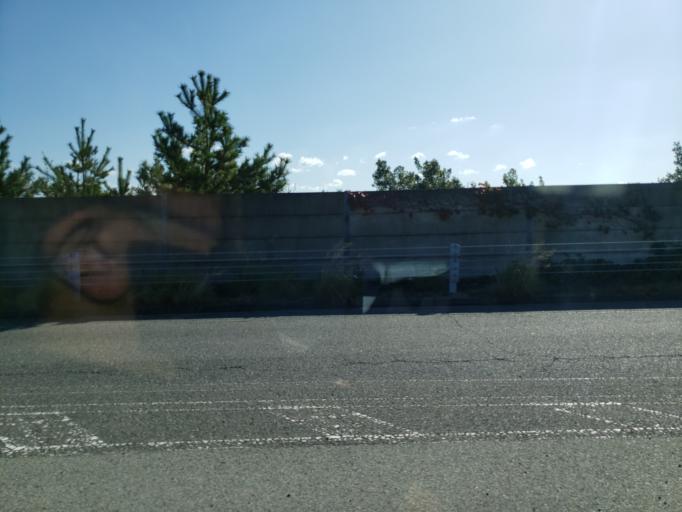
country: JP
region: Hyogo
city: Fukura
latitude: 34.3008
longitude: 134.7403
